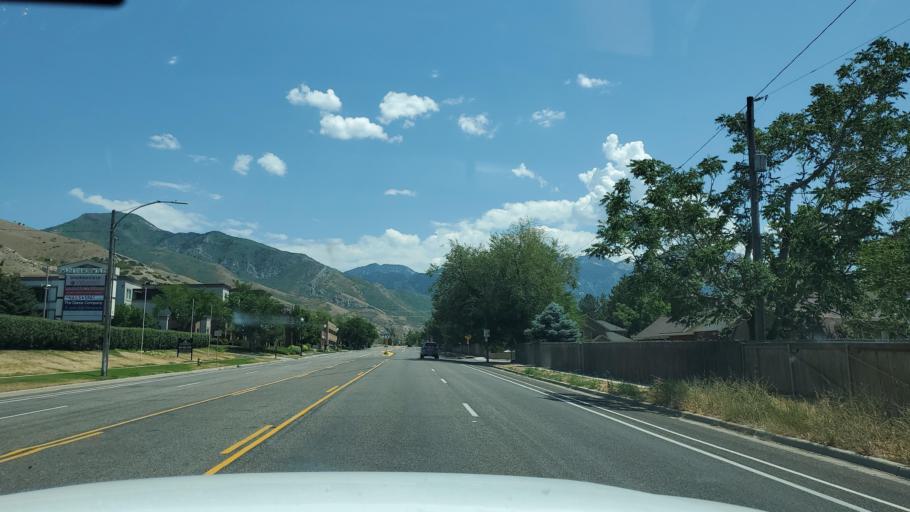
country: US
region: Utah
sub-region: Salt Lake County
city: Canyon Rim
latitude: 40.7206
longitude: -111.8171
